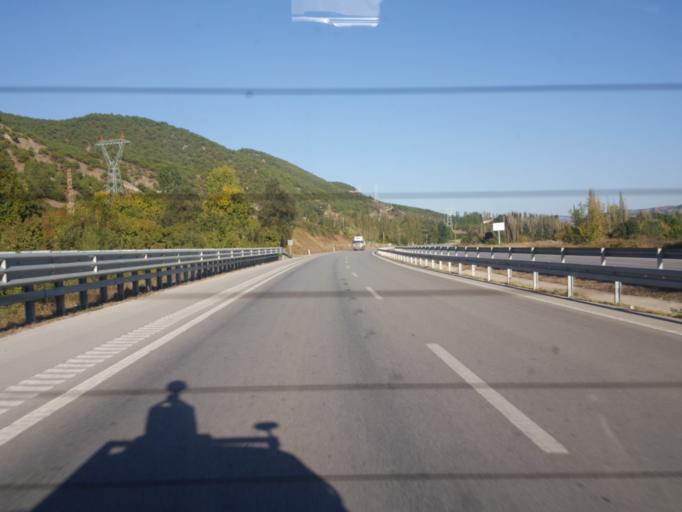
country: TR
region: Amasya
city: Tekke
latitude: 40.7386
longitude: 36.1691
